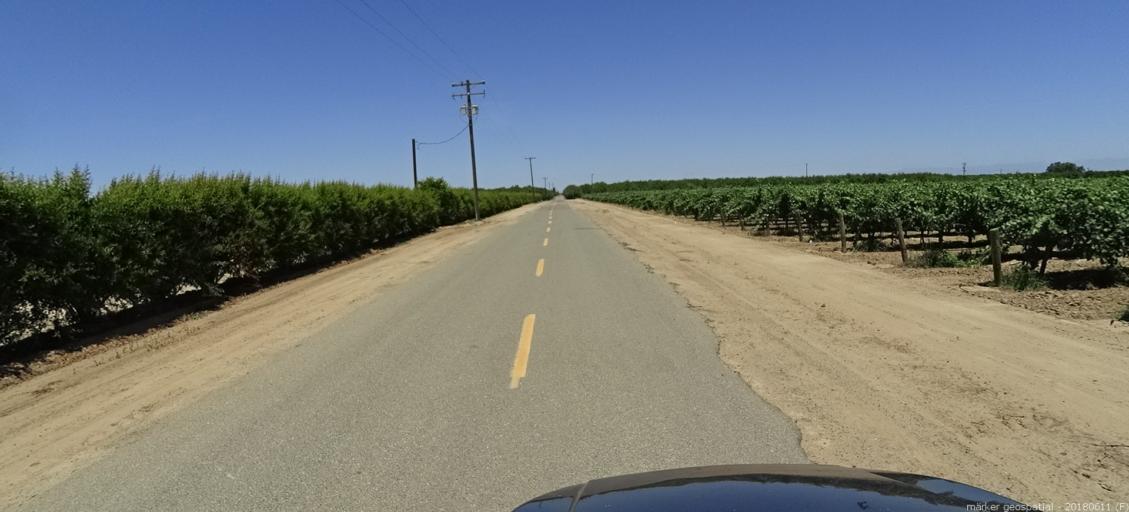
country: US
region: California
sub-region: Madera County
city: Fairmead
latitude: 37.0270
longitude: -120.1932
